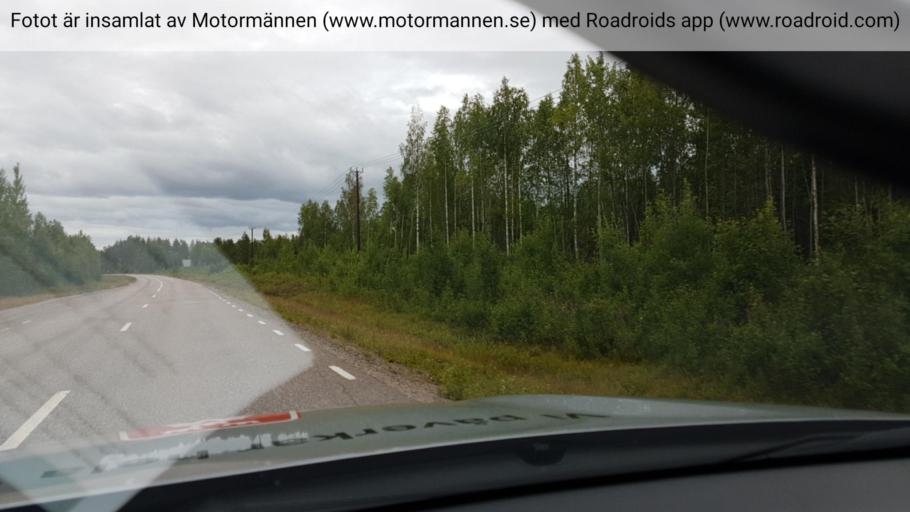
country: SE
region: Norrbotten
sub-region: Overkalix Kommun
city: OEverkalix
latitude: 66.7391
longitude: 22.8854
